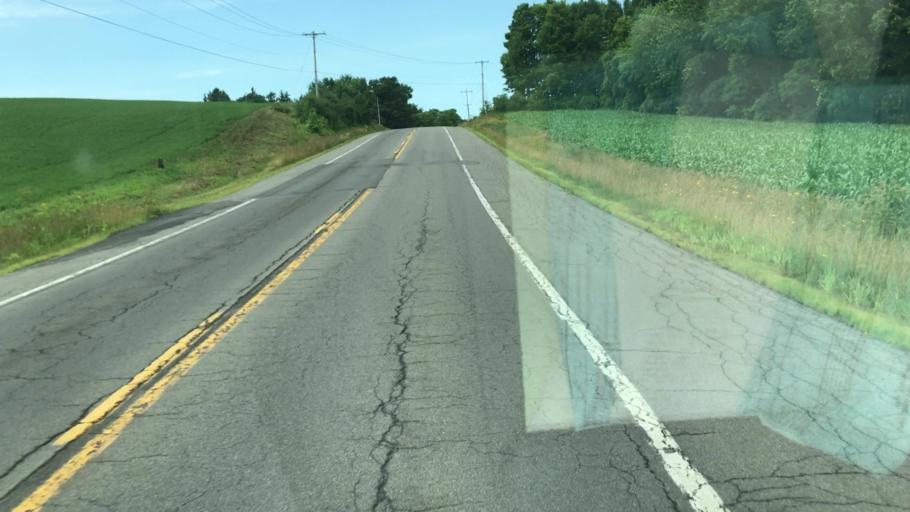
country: US
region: New York
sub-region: Onondaga County
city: Skaneateles
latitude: 42.9409
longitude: -76.3823
